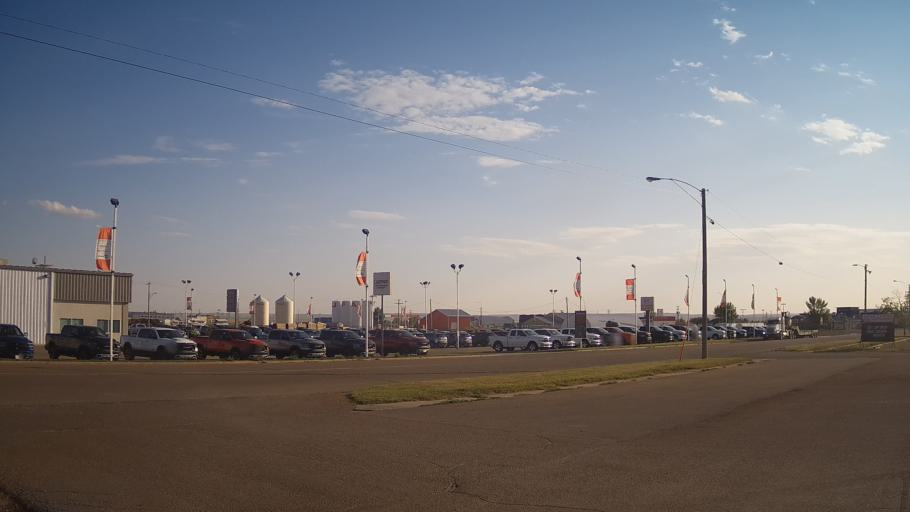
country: CA
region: Alberta
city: Hanna
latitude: 51.6410
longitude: -111.9393
